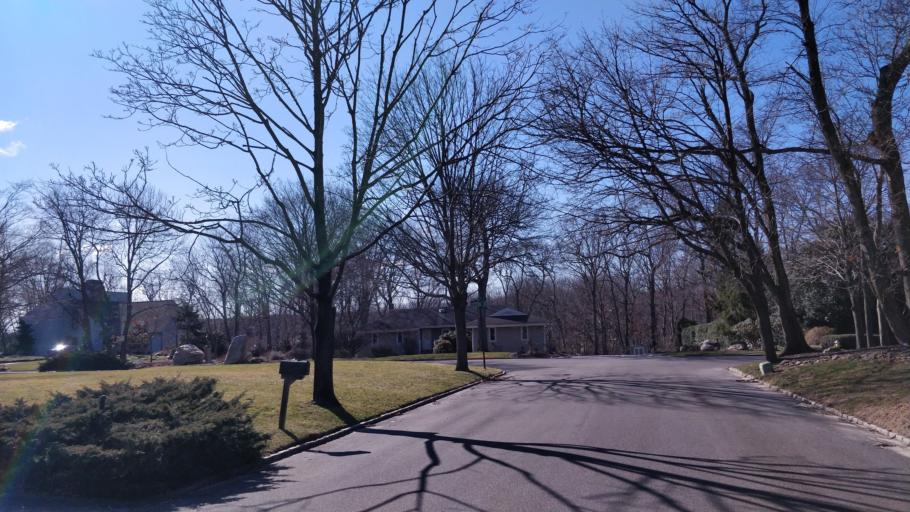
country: US
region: New York
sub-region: Suffolk County
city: Mount Sinai
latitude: 40.9602
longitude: -73.0455
